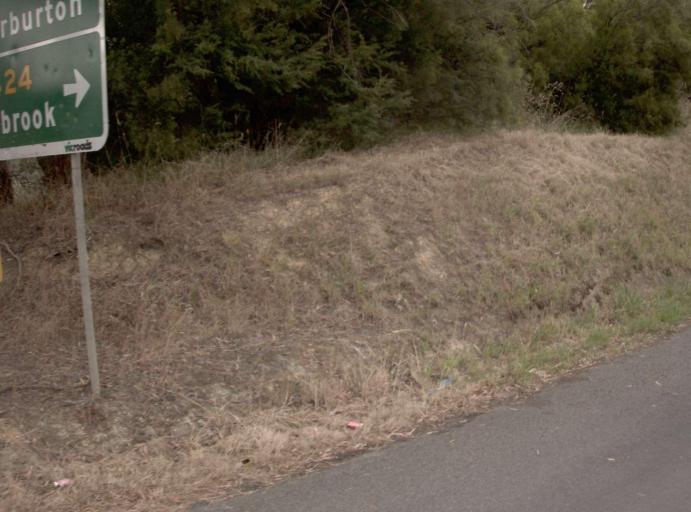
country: AU
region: Victoria
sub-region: Yarra Ranges
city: Launching Place
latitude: -37.7766
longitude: 145.5736
